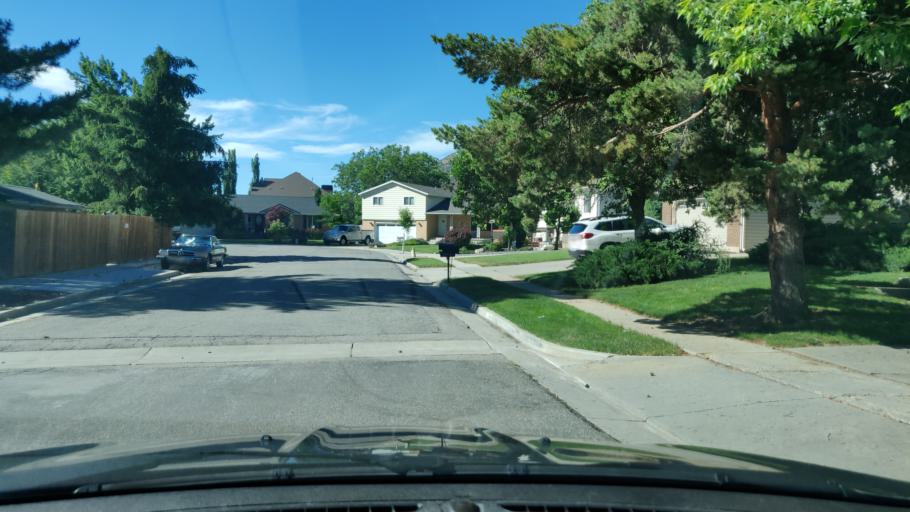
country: US
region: Utah
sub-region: Salt Lake County
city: Cottonwood Heights
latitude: 40.6219
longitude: -111.8025
